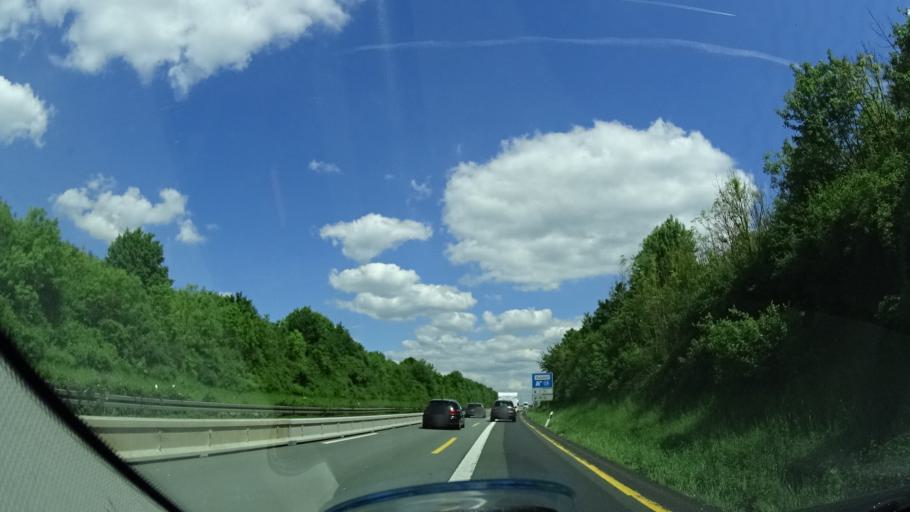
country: DE
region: North Rhine-Westphalia
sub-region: Regierungsbezirk Detmold
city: Paderborn
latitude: 51.6658
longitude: 8.7084
